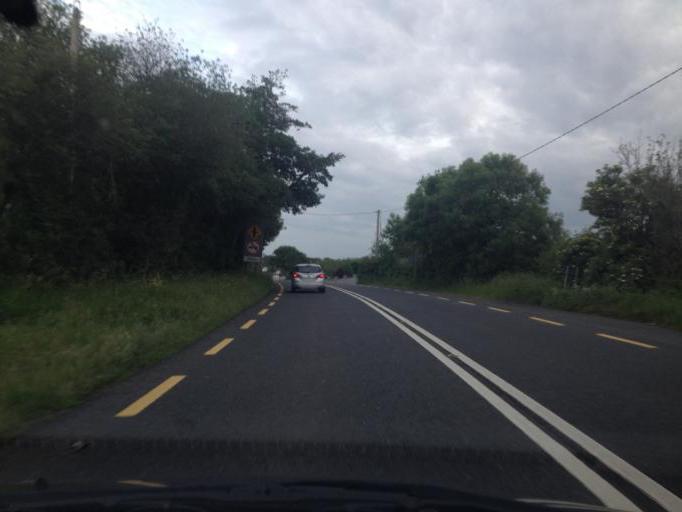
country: IE
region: Connaught
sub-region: Sligo
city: Sligo
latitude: 54.3441
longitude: -8.5040
